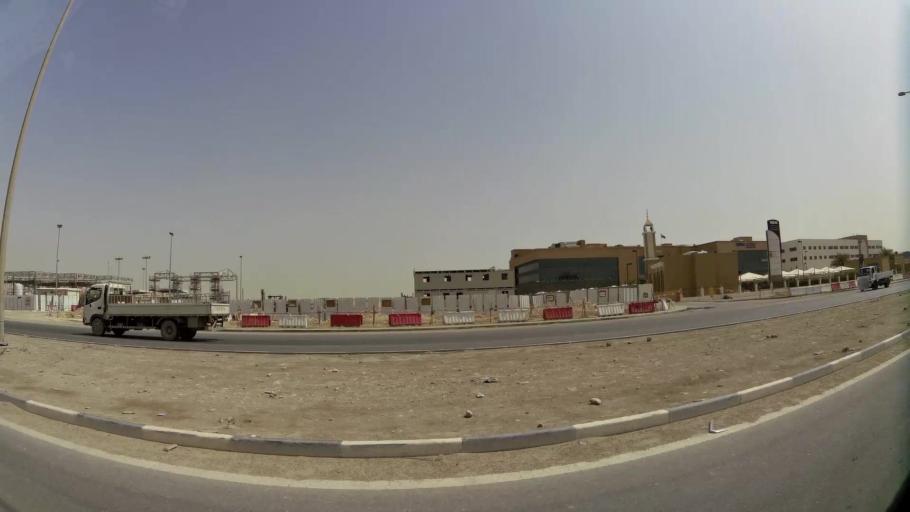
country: QA
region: Baladiyat ar Rayyan
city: Ar Rayyan
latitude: 25.1669
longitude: 51.4028
